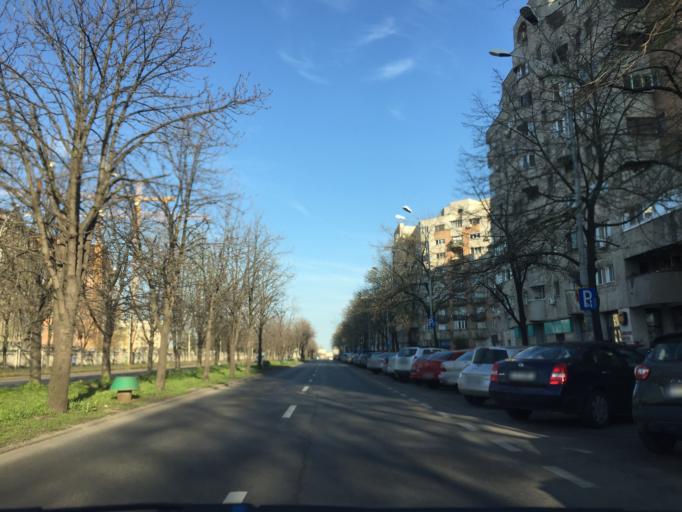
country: RO
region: Bucuresti
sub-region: Municipiul Bucuresti
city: Bucuresti
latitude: 44.4250
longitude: 26.0794
